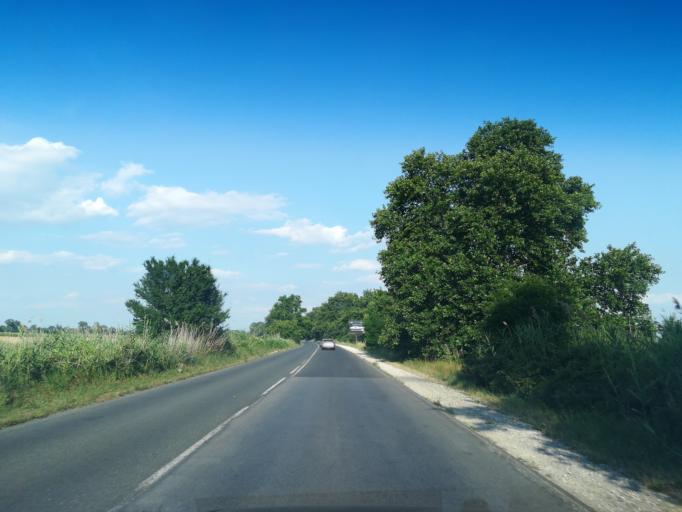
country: BG
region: Plovdiv
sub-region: Obshtina Sadovo
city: Sadovo
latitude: 42.1465
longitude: 24.8458
